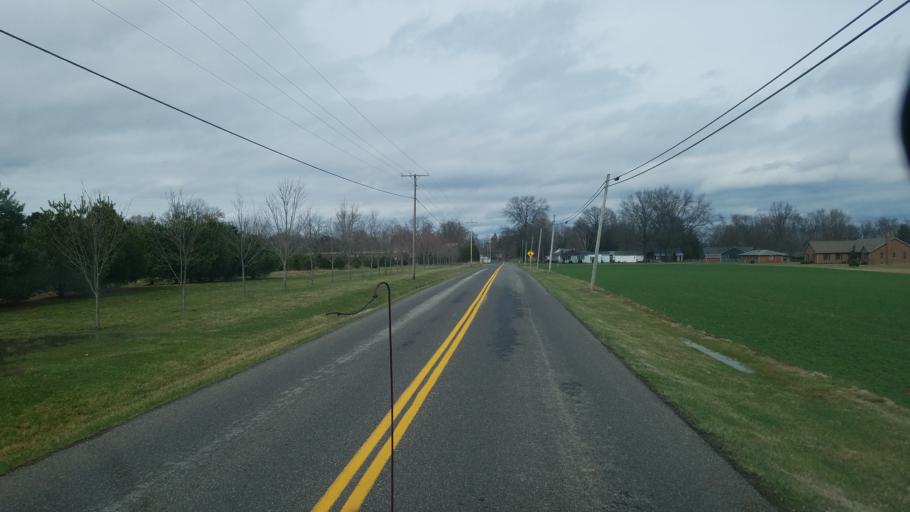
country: US
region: Ohio
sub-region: Wayne County
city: Wooster
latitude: 40.7751
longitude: -81.9633
